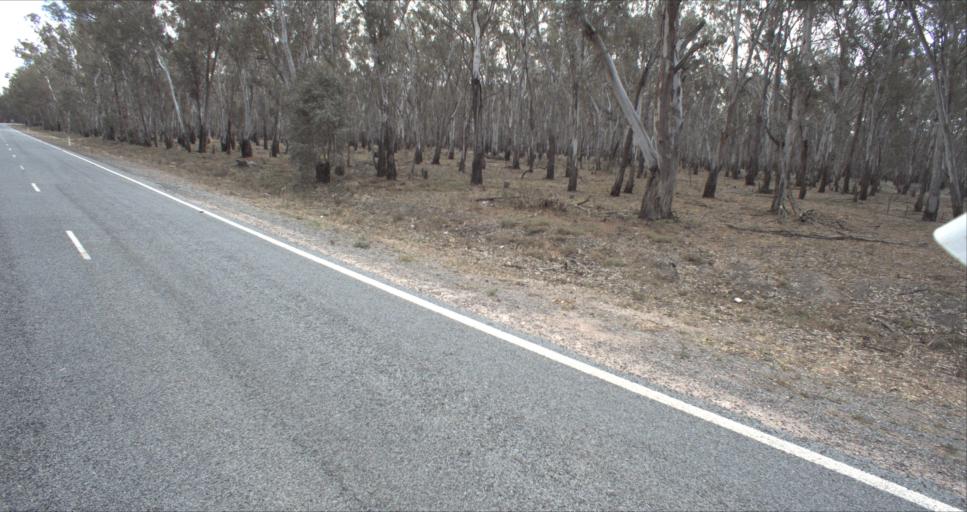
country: AU
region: New South Wales
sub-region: Leeton
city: Leeton
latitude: -34.6265
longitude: 146.3789
